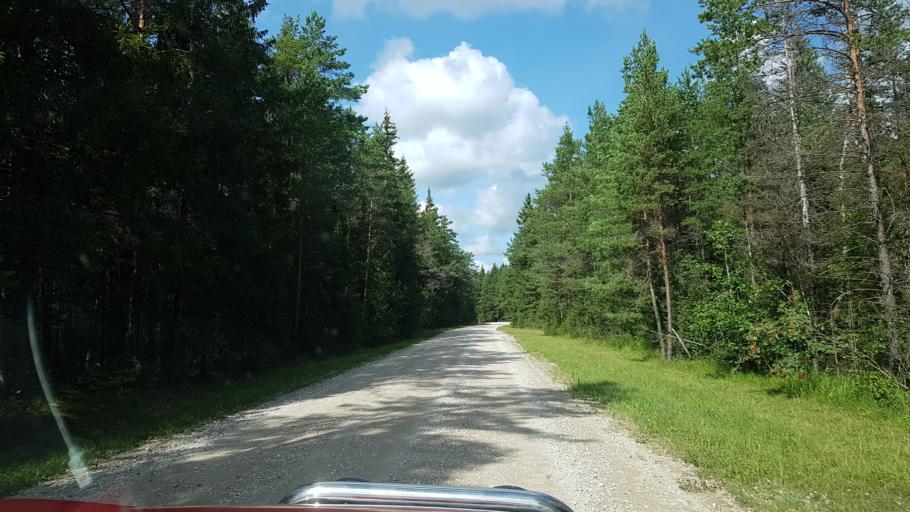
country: EE
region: Raplamaa
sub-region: Rapla vald
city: Rapla
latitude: 58.9643
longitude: 24.6381
